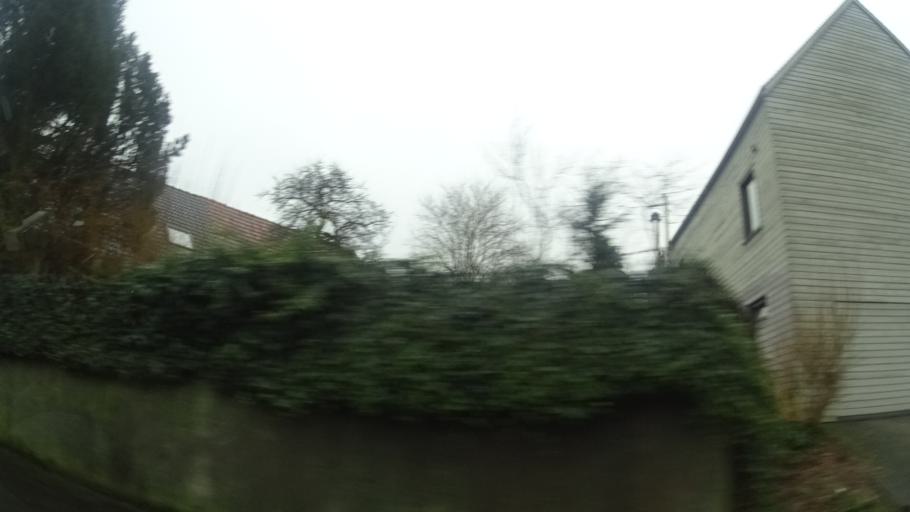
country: DE
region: Hesse
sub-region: Regierungsbezirk Kassel
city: Dipperz
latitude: 50.4870
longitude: 9.7982
